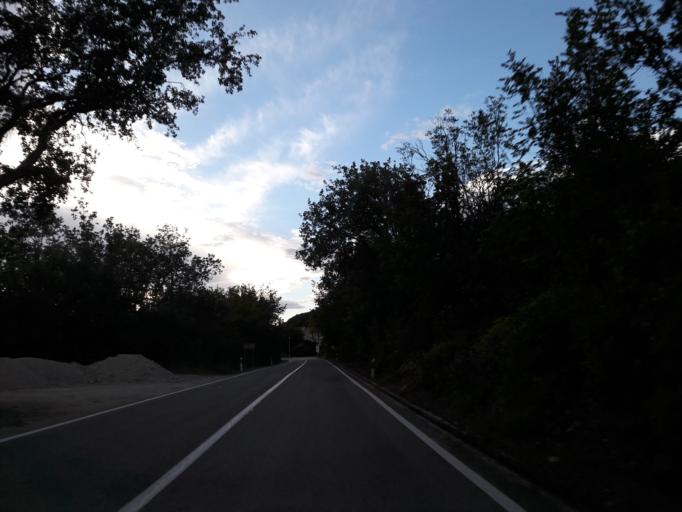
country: BA
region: Federation of Bosnia and Herzegovina
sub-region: Hercegovacko-Bosanski Kanton
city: Neum
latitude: 42.8815
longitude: 17.5097
